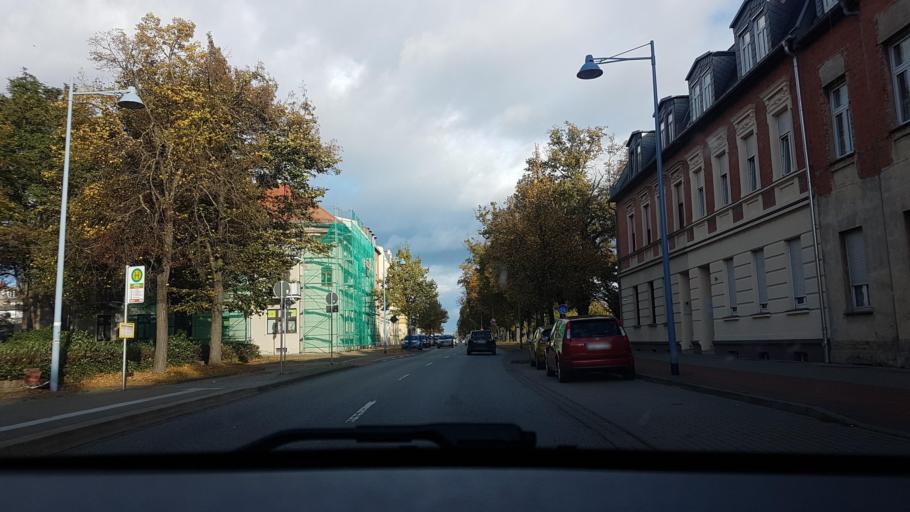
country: DE
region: Saxony-Anhalt
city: Bernburg
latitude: 51.7919
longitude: 11.7535
